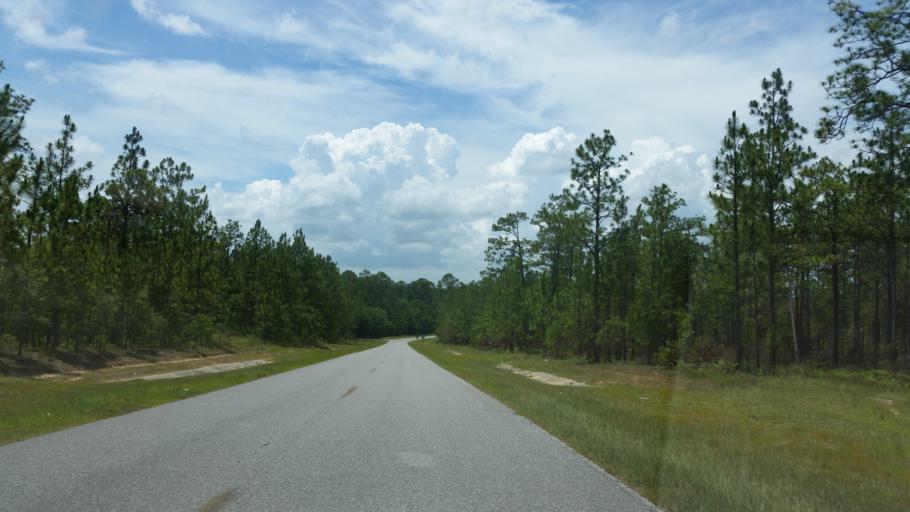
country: US
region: Florida
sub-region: Okaloosa County
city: Crestview
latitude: 30.7194
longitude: -86.7837
